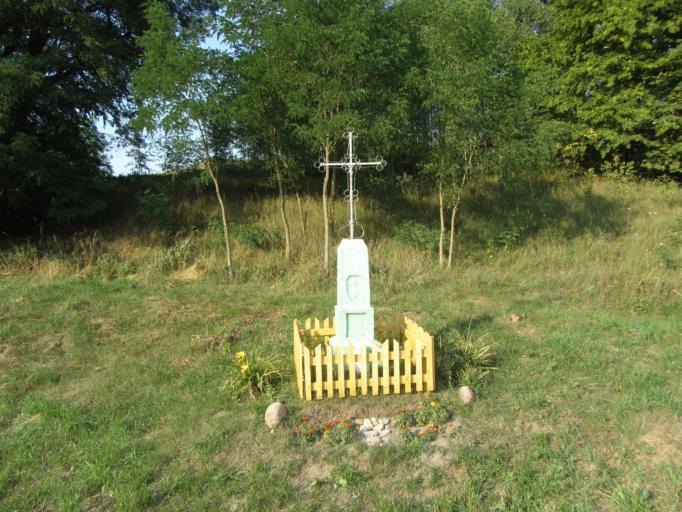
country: LT
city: Lazdijai
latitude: 54.0960
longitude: 23.5522
